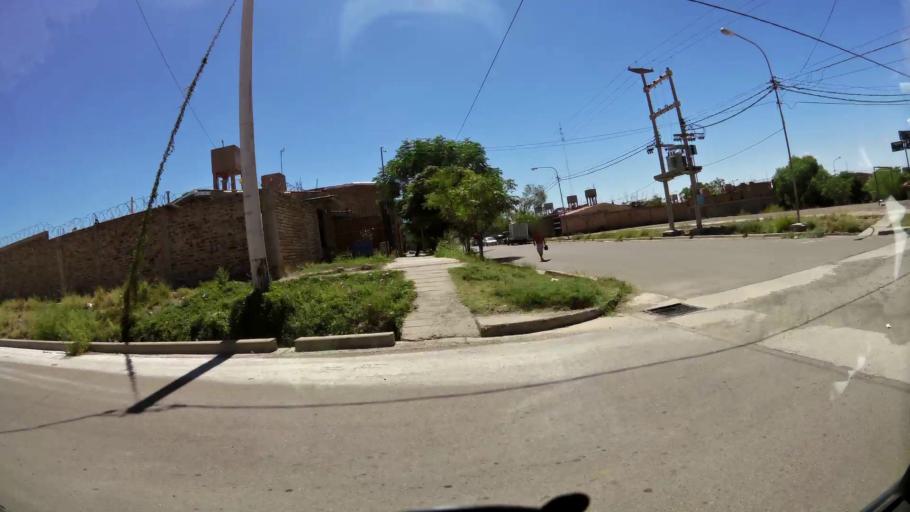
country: AR
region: Mendoza
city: Las Heras
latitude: -32.8512
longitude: -68.8649
